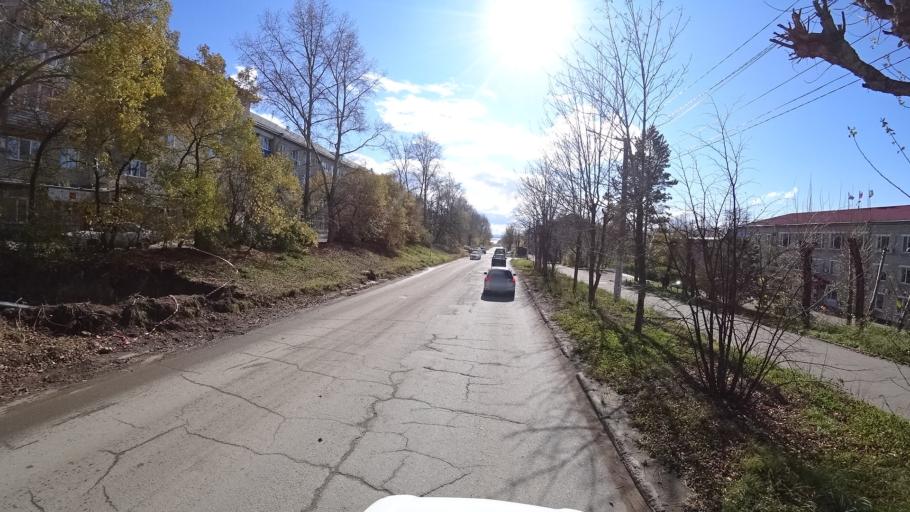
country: RU
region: Khabarovsk Krai
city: Amursk
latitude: 50.2193
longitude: 136.9032
